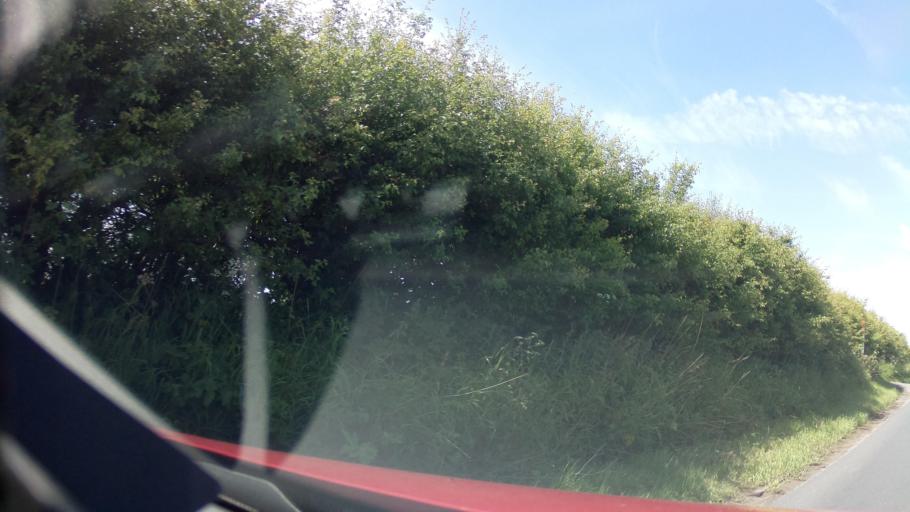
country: GB
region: England
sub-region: North Lincolnshire
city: Redbourne
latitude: 53.5013
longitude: -0.5566
